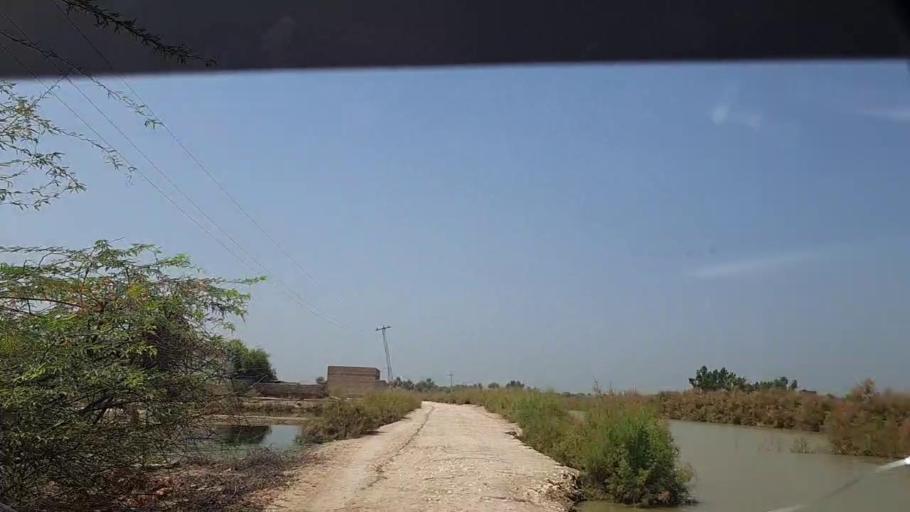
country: PK
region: Sindh
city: Ghauspur
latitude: 28.1877
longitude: 69.0981
